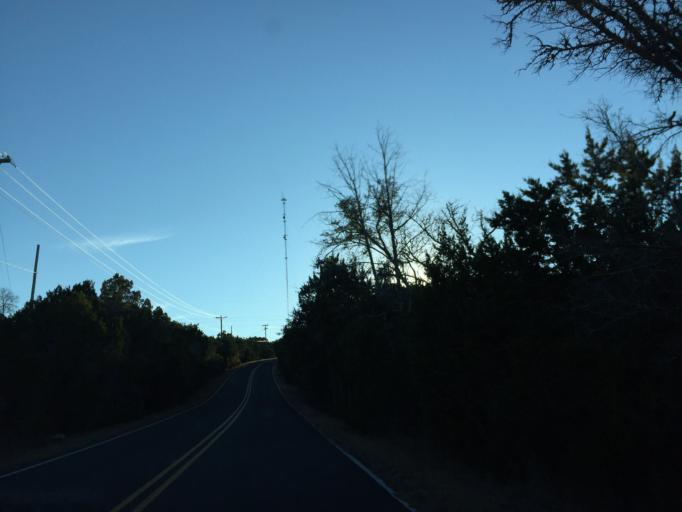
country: US
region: Texas
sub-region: Travis County
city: Lago Vista
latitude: 30.5063
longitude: -98.0492
